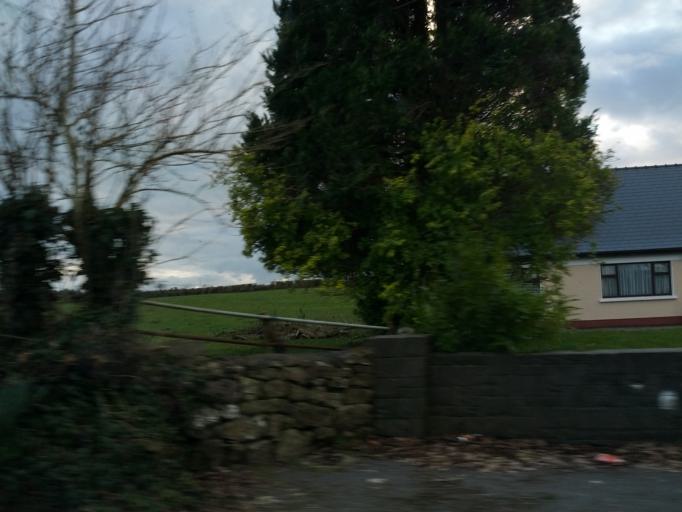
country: IE
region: Connaught
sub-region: County Galway
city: Athenry
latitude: 53.4377
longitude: -8.7205
